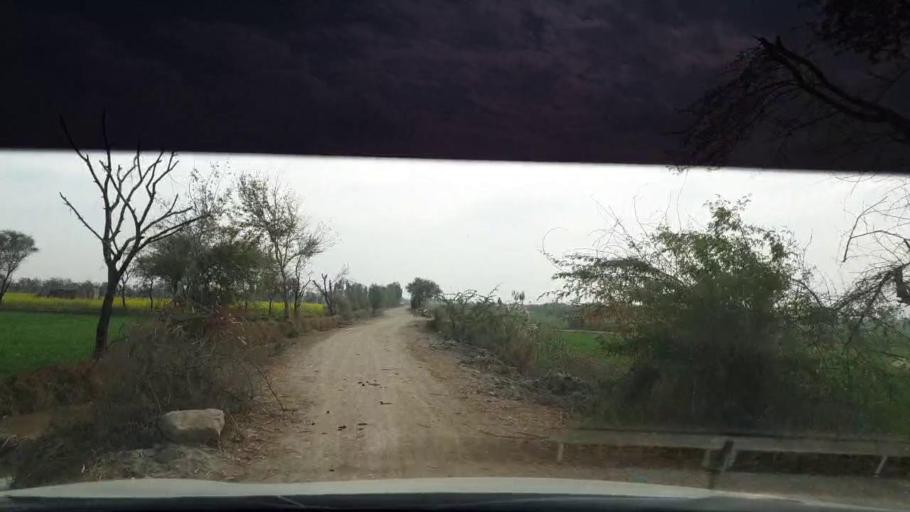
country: PK
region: Sindh
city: Berani
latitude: 25.7533
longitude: 68.8769
